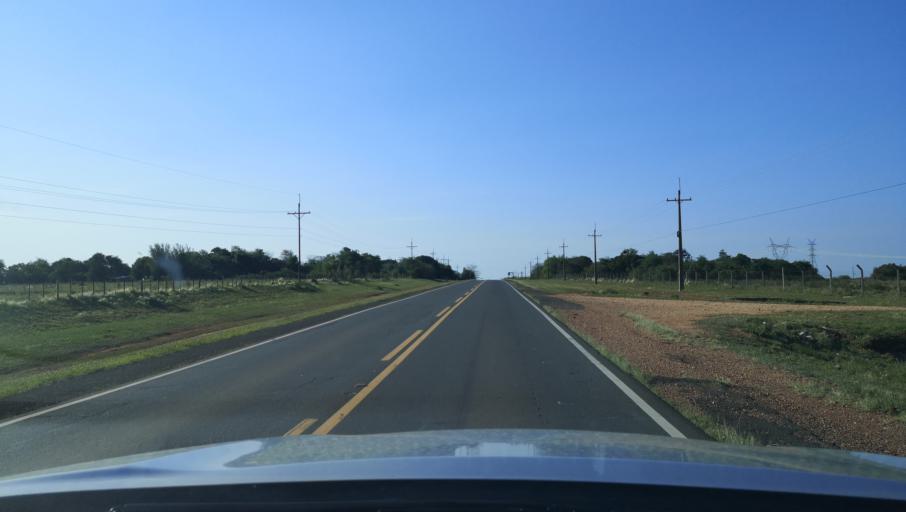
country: PY
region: Misiones
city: Santa Maria
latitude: -26.8021
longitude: -57.0212
